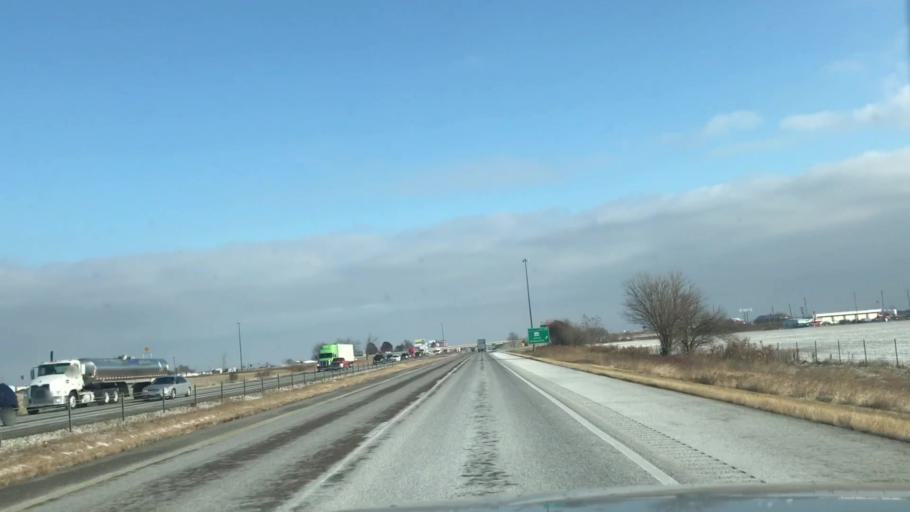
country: US
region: Illinois
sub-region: Madison County
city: Worden
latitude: 38.8837
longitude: -89.8418
